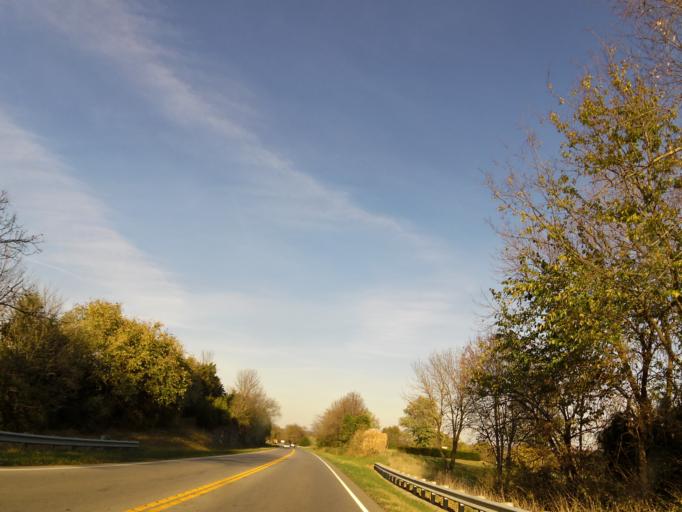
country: US
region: Kentucky
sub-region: Lincoln County
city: Stanford
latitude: 37.5567
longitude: -84.6311
